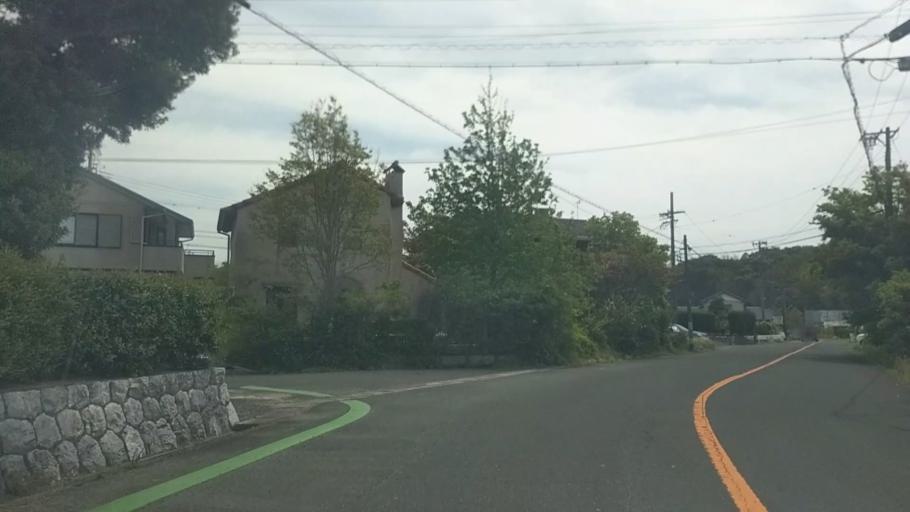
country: JP
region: Shizuoka
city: Kosai-shi
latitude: 34.7552
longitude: 137.5123
